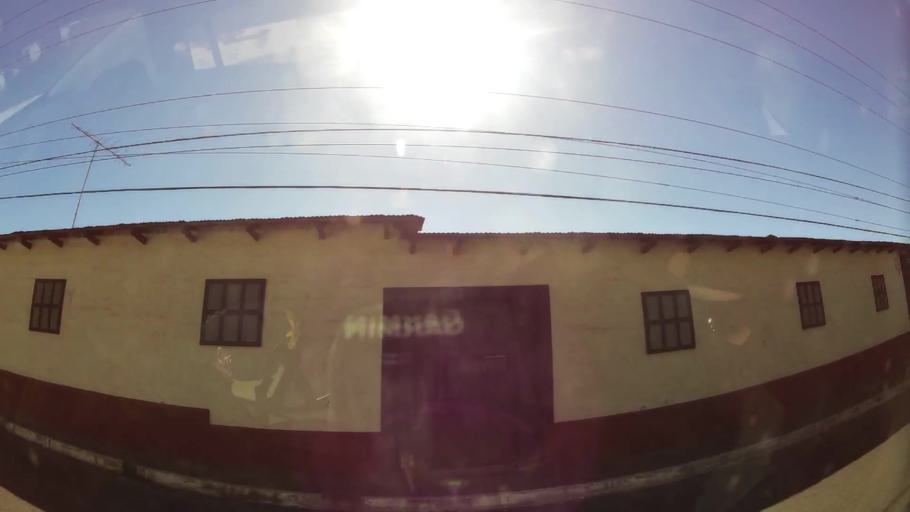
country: SV
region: Sonsonate
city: Juayua
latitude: 13.8422
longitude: -89.7496
